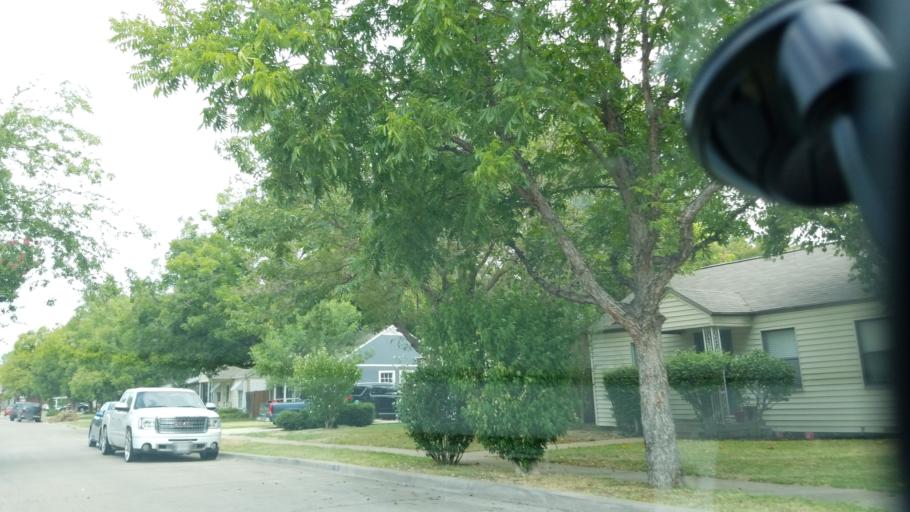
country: US
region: Texas
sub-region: Dallas County
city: Grand Prairie
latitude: 32.7521
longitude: -96.9843
